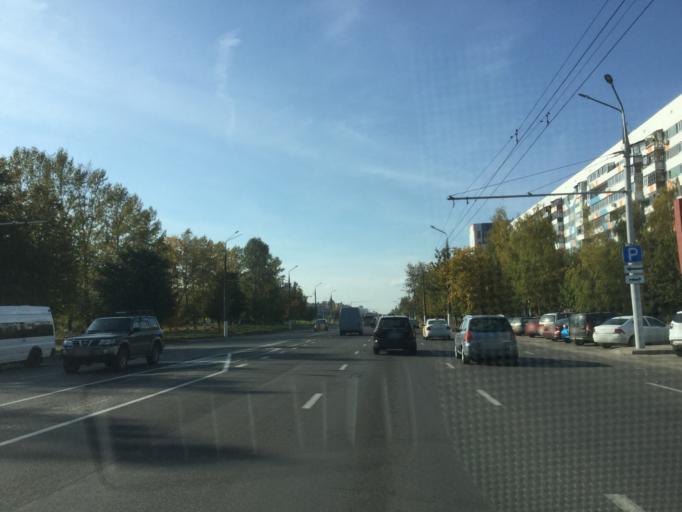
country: BY
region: Vitebsk
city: Vitebsk
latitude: 55.1689
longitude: 30.2363
